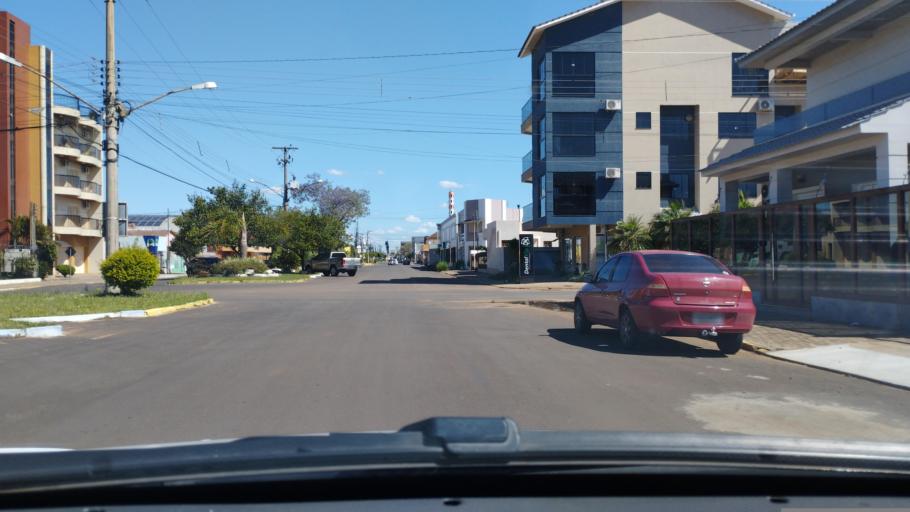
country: BR
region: Rio Grande do Sul
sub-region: Tupancireta
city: Tupancireta
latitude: -29.0759
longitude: -53.8391
